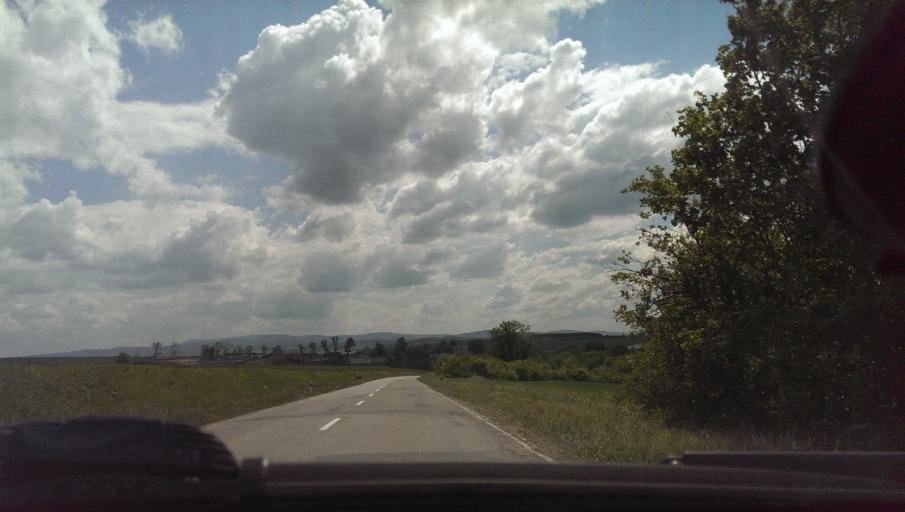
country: CZ
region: Zlin
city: Kunovice
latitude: 49.0109
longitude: 17.4894
